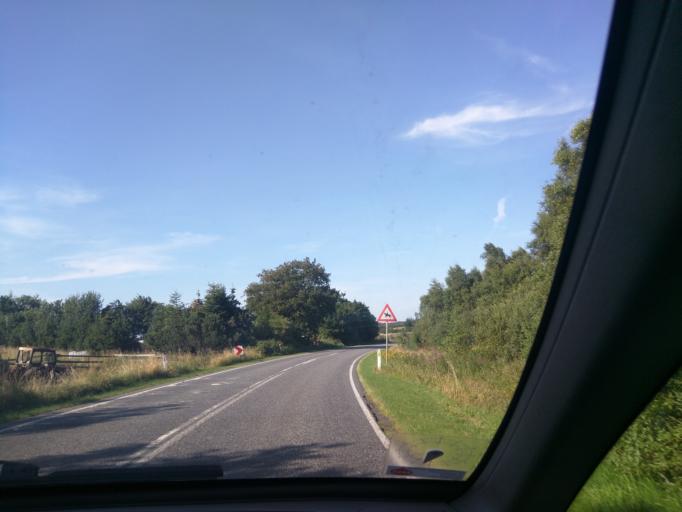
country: DK
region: Central Jutland
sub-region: Viborg Kommune
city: Bjerringbro
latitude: 56.4202
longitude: 9.6698
